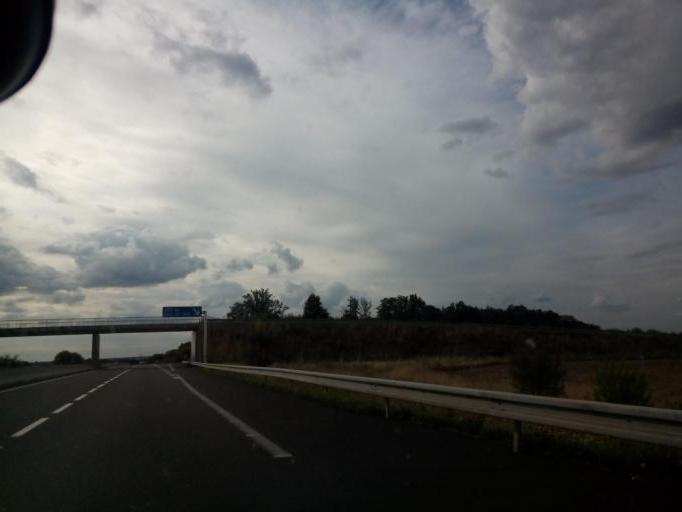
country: FR
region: Centre
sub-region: Departement du Loir-et-Cher
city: Faverolles-sur-Cher
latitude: 47.2990
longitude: 1.2294
